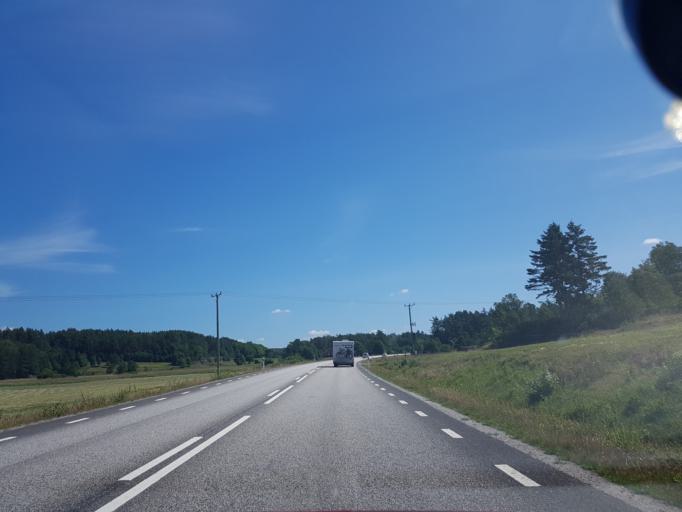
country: SE
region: Vaestra Goetaland
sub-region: Orust
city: Henan
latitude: 58.1463
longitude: 11.6194
